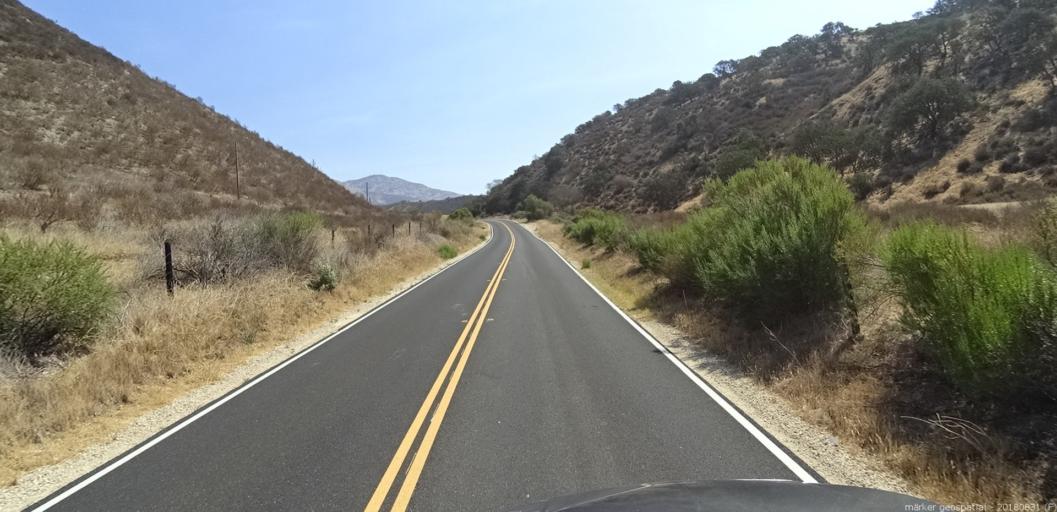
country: US
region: California
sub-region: Monterey County
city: Soledad
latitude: 36.4235
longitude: -121.2392
